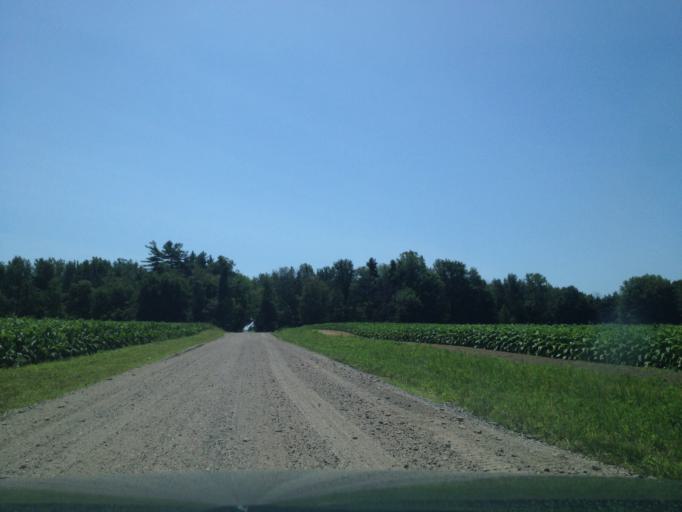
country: CA
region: Ontario
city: Aylmer
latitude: 42.6492
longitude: -80.7705
